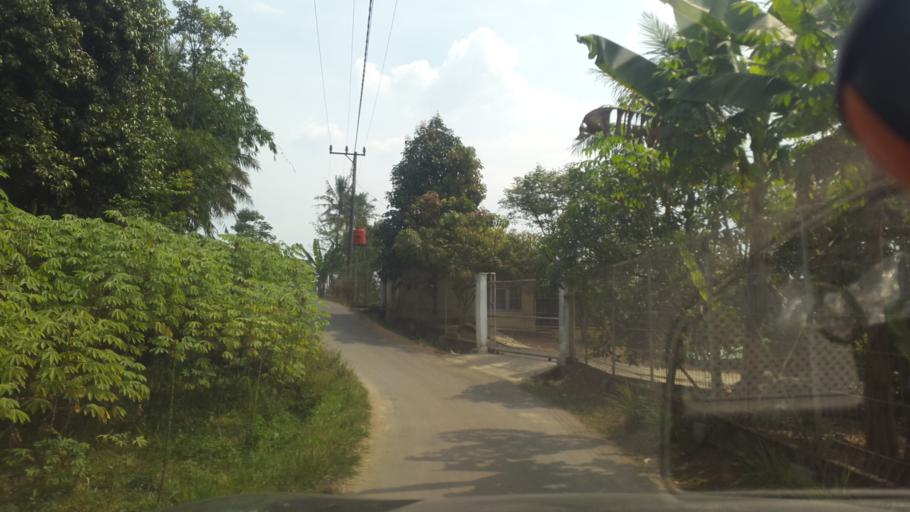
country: ID
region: West Java
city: Cicurug
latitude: -6.8054
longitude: 106.8001
